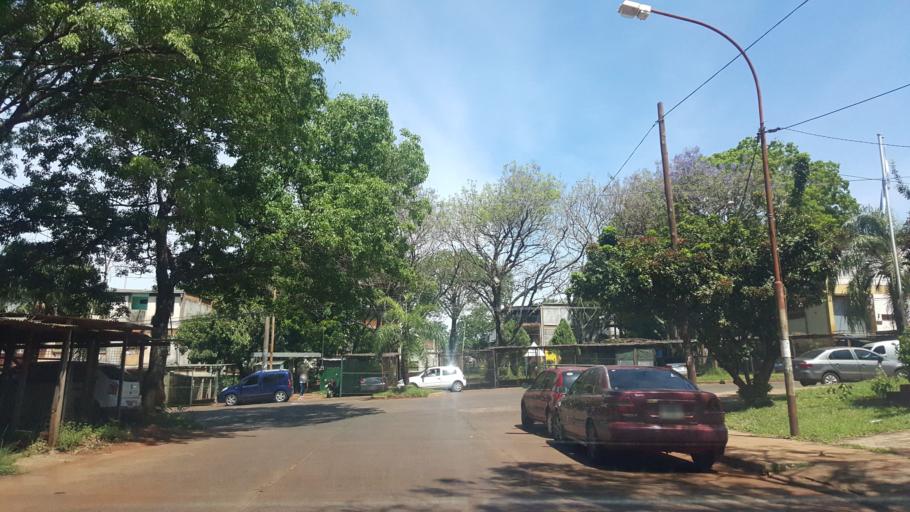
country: AR
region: Misiones
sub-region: Departamento de Capital
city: Posadas
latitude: -27.3968
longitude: -55.9066
